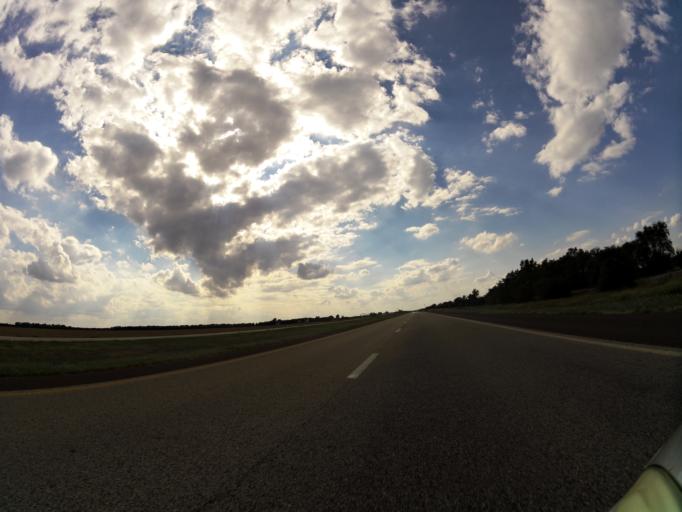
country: US
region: Kansas
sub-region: Reno County
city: South Hutchinson
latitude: 37.9512
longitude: -97.8939
